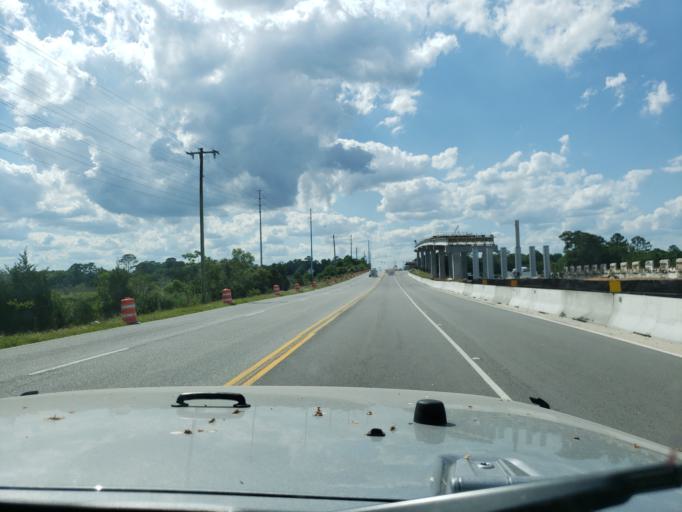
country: US
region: Georgia
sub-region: Chatham County
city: Whitemarsh Island
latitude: 32.0598
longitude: -81.0250
